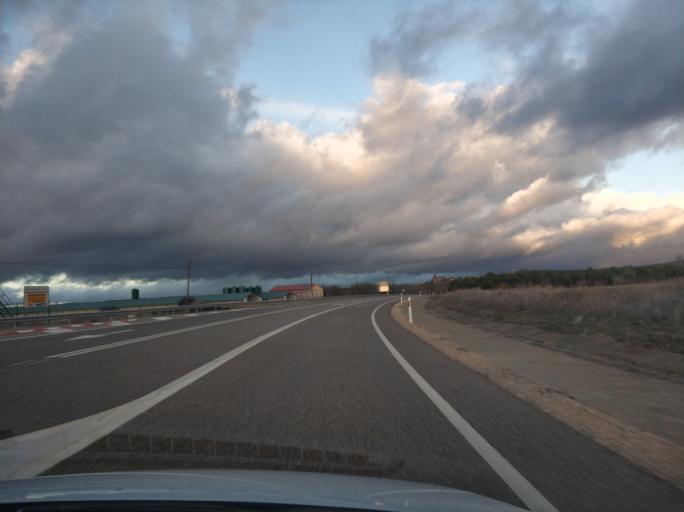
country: ES
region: Castille and Leon
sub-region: Provincia de Segovia
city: Ayllon
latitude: 41.4068
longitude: -3.4157
